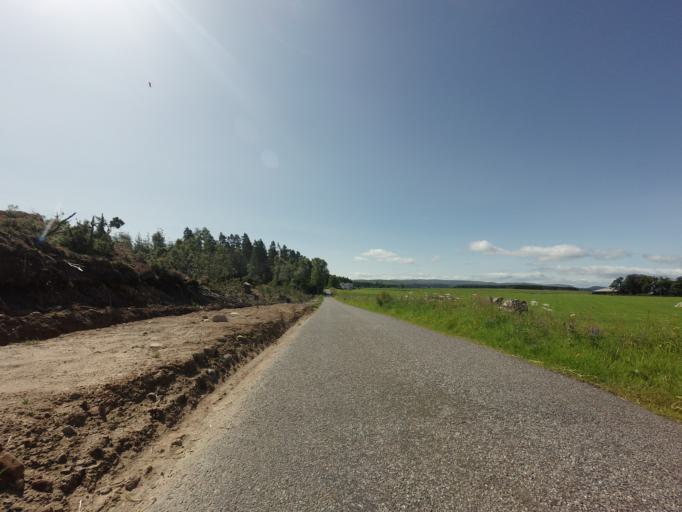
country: GB
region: Scotland
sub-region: Highland
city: Nairn
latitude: 57.5290
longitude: -3.8622
